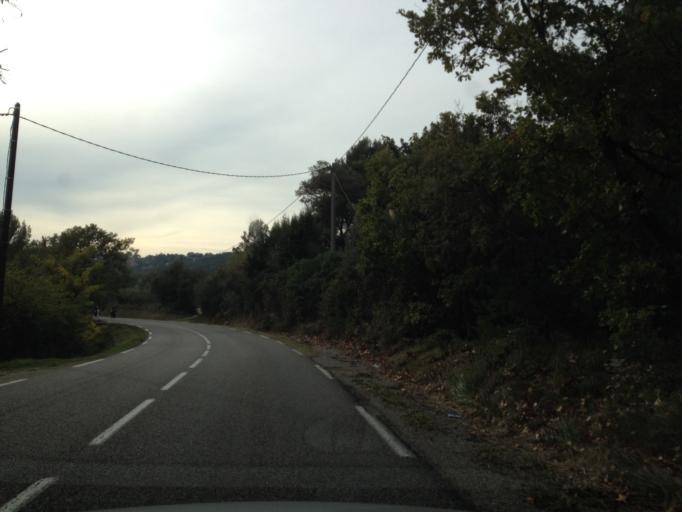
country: FR
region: Provence-Alpes-Cote d'Azur
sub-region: Departement du Var
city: Salernes
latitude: 43.5727
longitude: 6.2028
